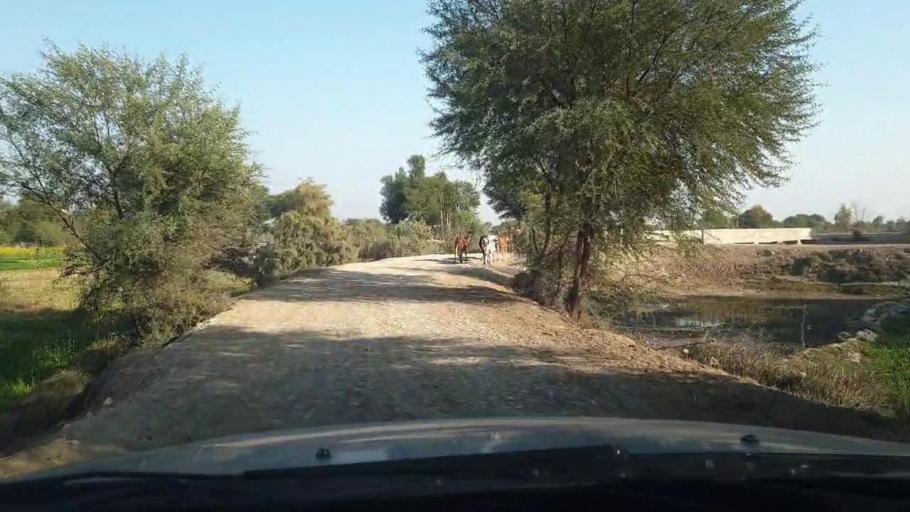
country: PK
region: Sindh
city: Mirpur Mathelo
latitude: 27.9738
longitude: 69.5266
